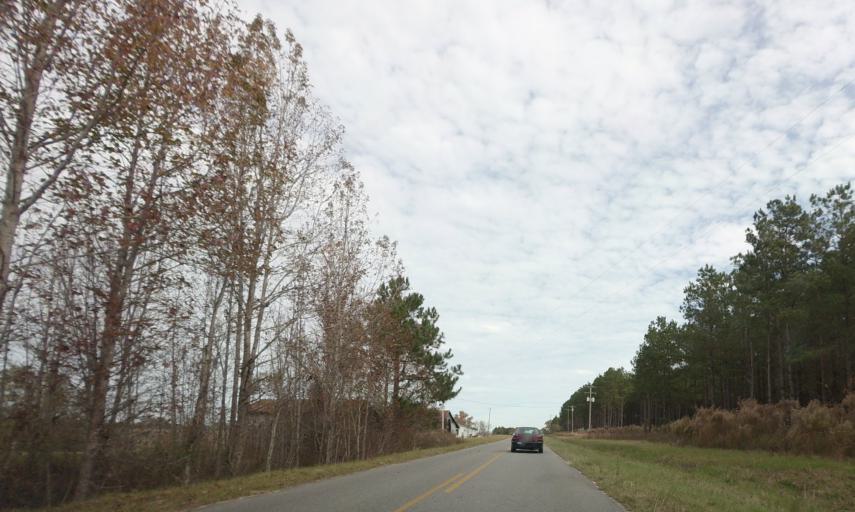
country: US
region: Georgia
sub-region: Dodge County
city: Chester
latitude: 32.4171
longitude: -83.1918
